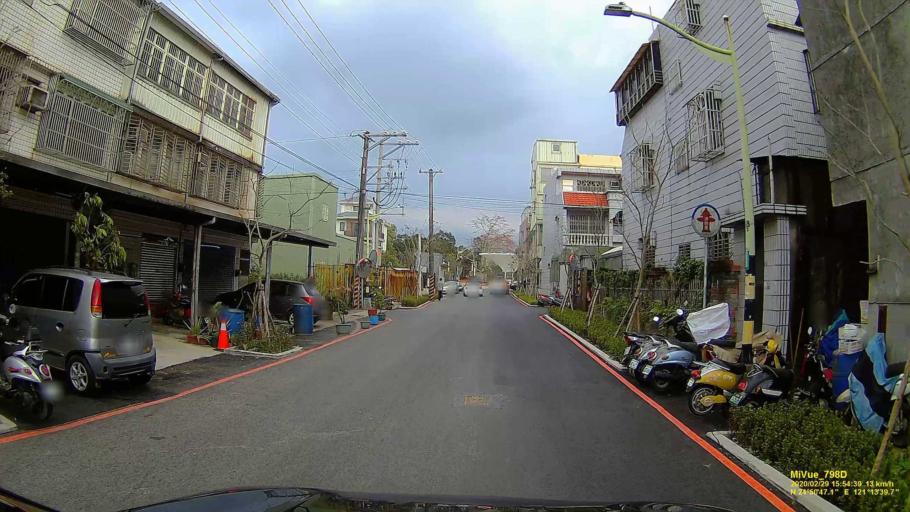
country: TW
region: Taiwan
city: Daxi
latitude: 24.8463
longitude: 121.2277
